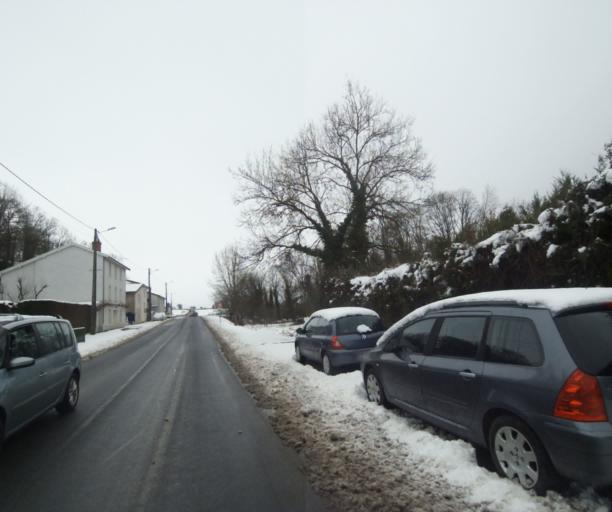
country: FR
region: Champagne-Ardenne
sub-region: Departement de la Haute-Marne
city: Wassy
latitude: 48.4753
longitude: 4.9704
